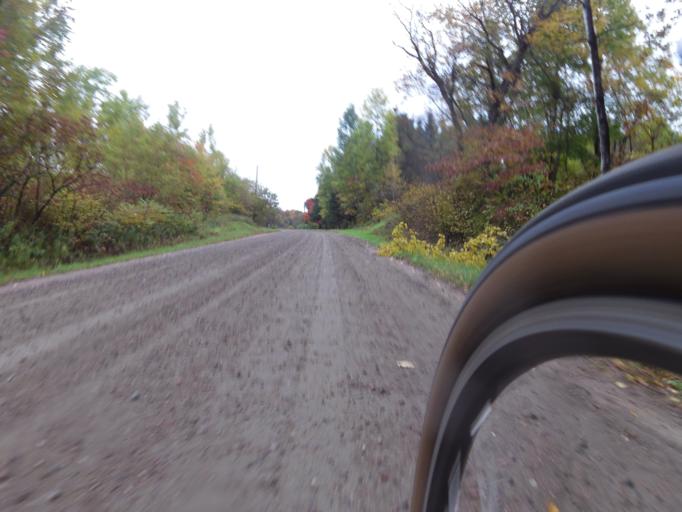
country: CA
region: Quebec
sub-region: Outaouais
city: Shawville
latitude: 45.6846
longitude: -76.5607
